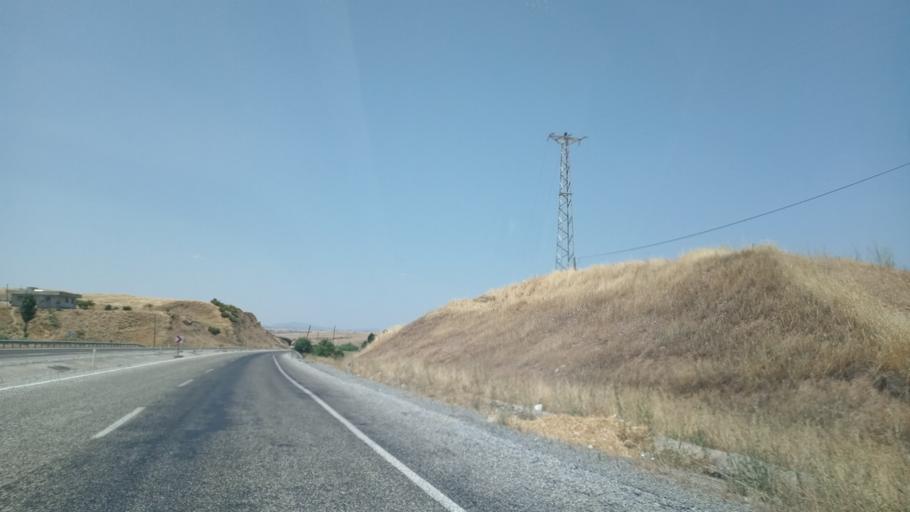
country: TR
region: Batman
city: Bekirhan
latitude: 38.1548
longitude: 41.3564
